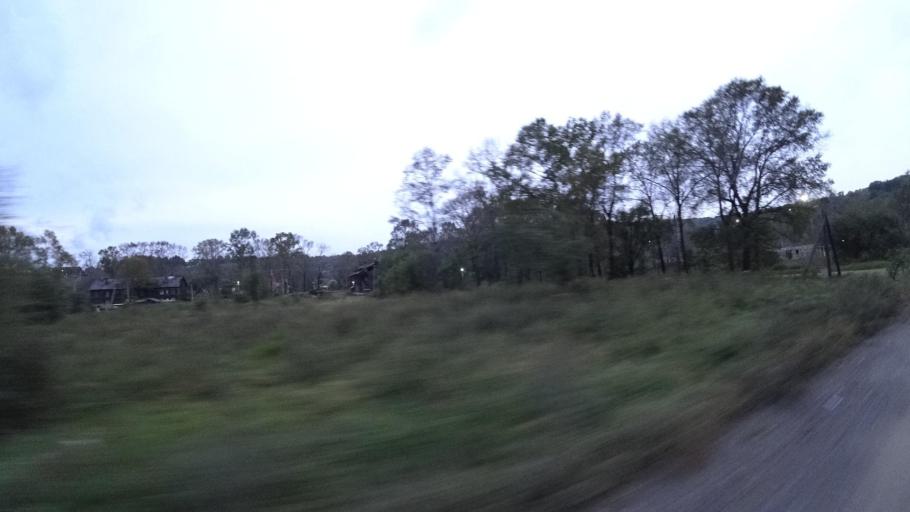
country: RU
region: Jewish Autonomous Oblast
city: Izvestkovyy
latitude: 48.9864
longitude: 131.5469
